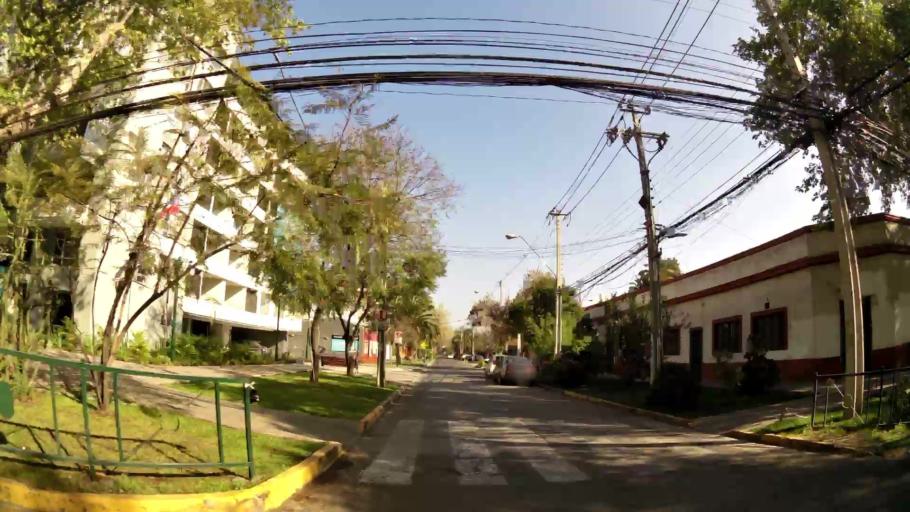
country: CL
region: Santiago Metropolitan
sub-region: Provincia de Santiago
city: Villa Presidente Frei, Nunoa, Santiago, Chile
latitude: -33.4568
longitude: -70.5959
